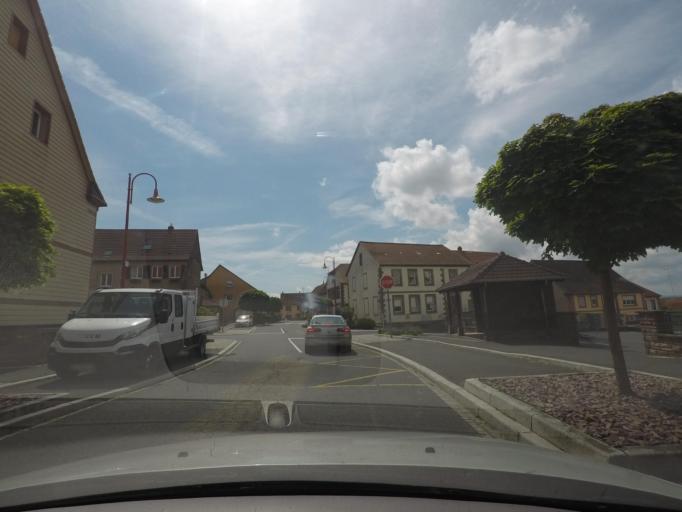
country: FR
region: Alsace
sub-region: Departement du Bas-Rhin
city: Drulingen
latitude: 48.8298
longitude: 7.2351
